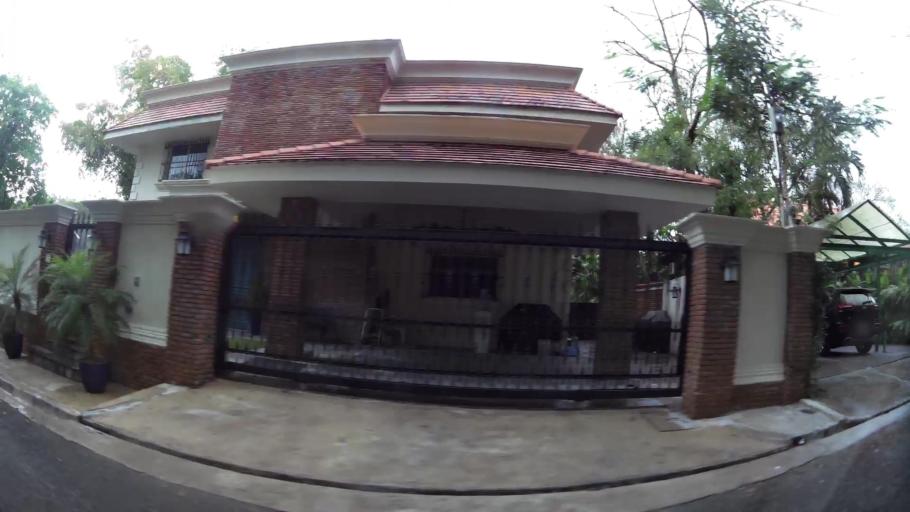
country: DO
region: Nacional
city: La Agustina
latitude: 18.5122
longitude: -69.9521
